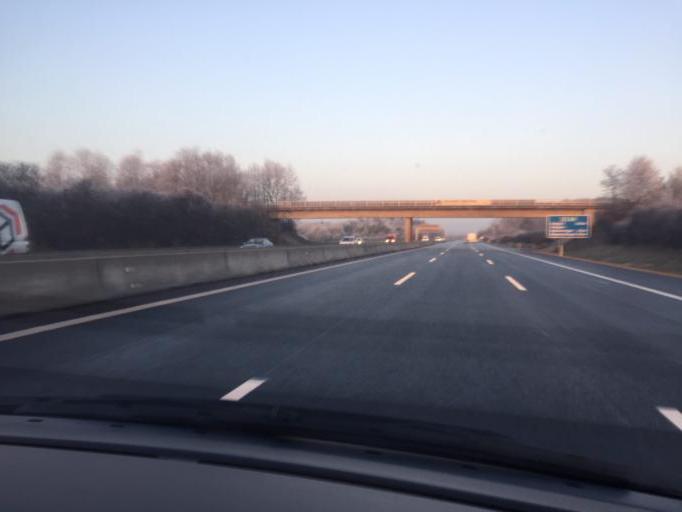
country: DE
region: Baden-Wuerttemberg
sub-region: Freiburg Region
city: Aach
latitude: 47.8206
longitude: 8.8409
